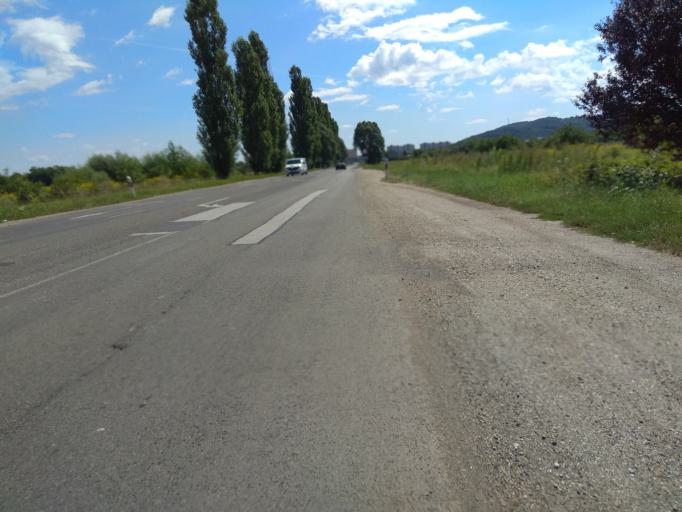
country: HU
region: Borsod-Abauj-Zemplen
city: Kazincbarcika
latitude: 48.2636
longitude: 20.6115
